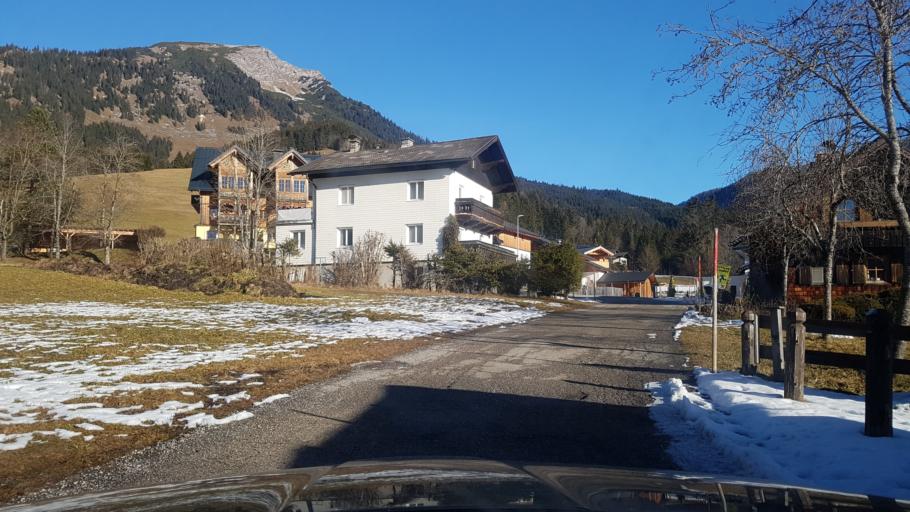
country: AT
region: Salzburg
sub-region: Politischer Bezirk Salzburg-Umgebung
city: Strobl
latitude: 47.5947
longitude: 13.4675
